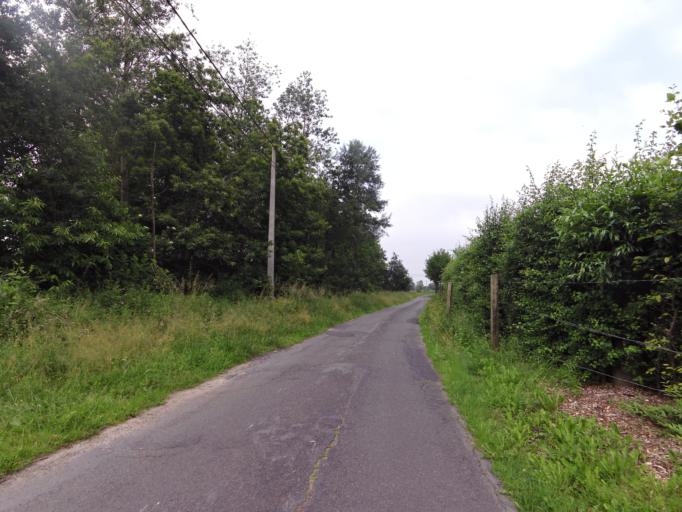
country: BE
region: Flanders
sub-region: Provincie West-Vlaanderen
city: Jabbeke
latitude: 51.1389
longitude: 3.0800
